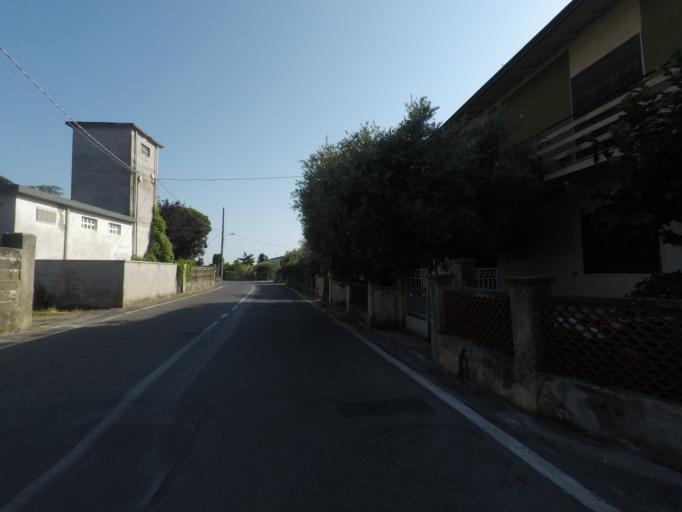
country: IT
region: Liguria
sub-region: Provincia di La Spezia
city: Casano-Dogana-Isola
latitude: 44.0644
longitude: 10.0308
